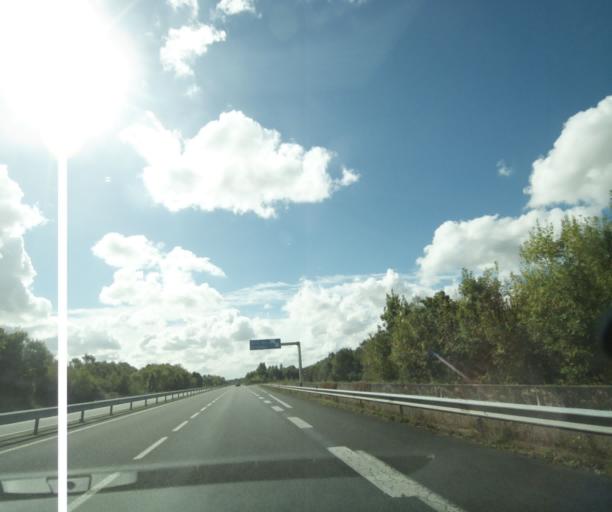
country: FR
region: Poitou-Charentes
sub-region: Departement de la Charente-Maritime
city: Saint-Savinien
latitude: 45.8703
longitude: -0.7335
